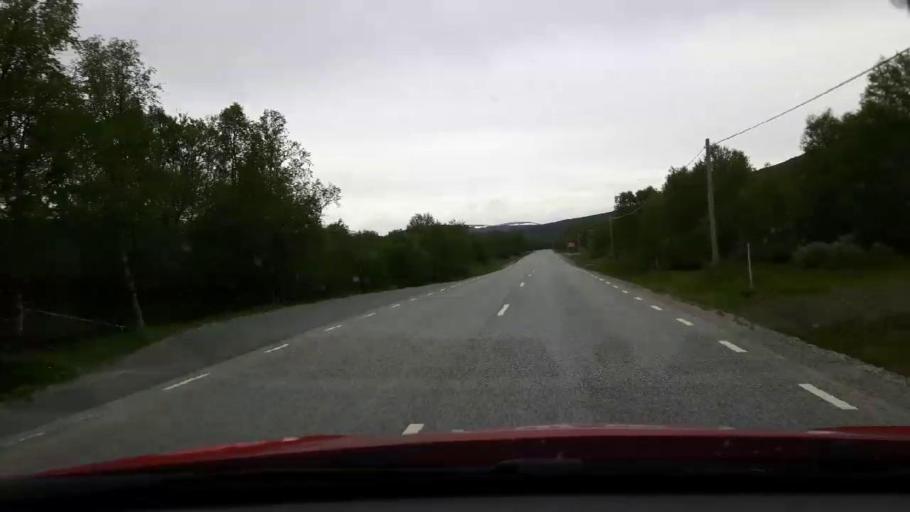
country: NO
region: Sor-Trondelag
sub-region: Tydal
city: Aas
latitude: 62.6896
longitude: 12.4108
